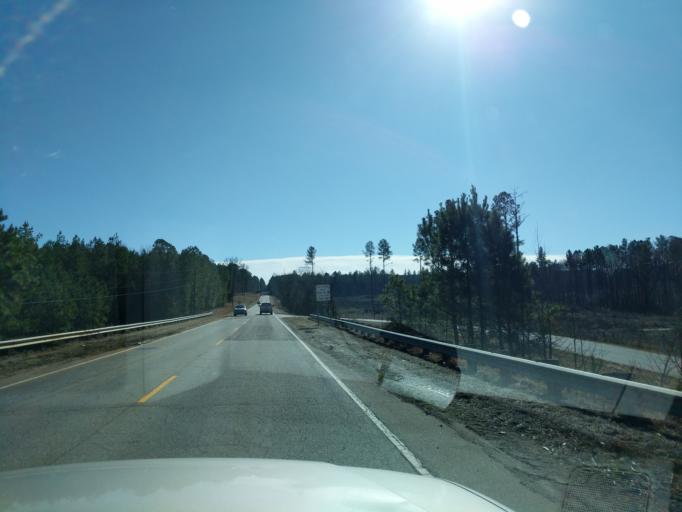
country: US
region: South Carolina
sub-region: Greenwood County
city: Ninety Six
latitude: 34.1722
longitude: -81.8623
